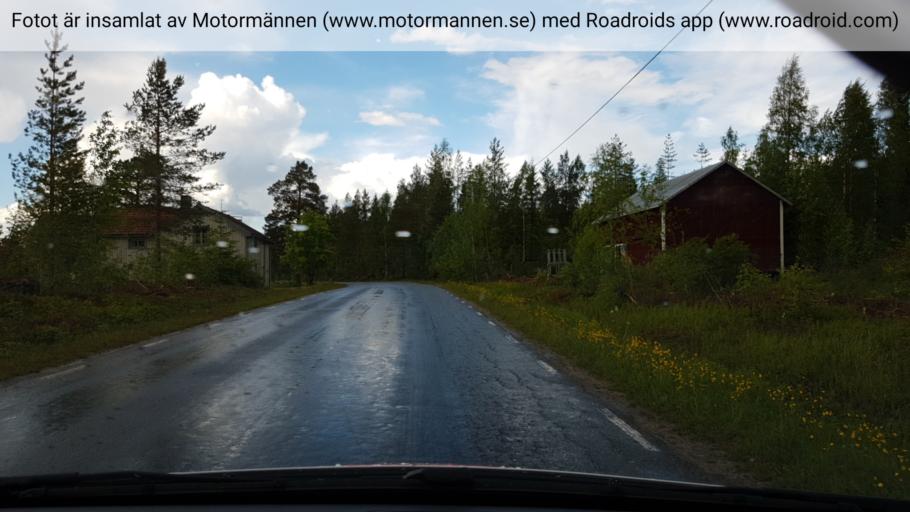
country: SE
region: Vaesterbotten
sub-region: Umea Kommun
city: Roback
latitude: 63.9977
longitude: 20.1002
